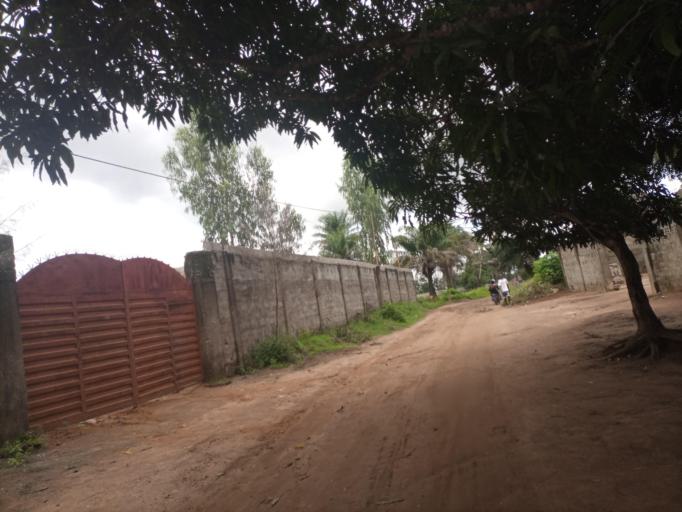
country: SL
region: Northern Province
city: Masoyila
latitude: 8.5950
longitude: -13.1637
